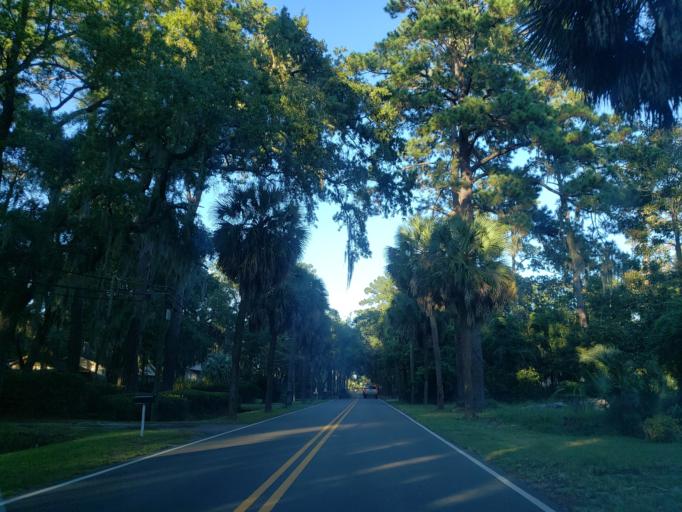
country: US
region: Georgia
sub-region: Chatham County
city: Isle of Hope
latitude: 31.9960
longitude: -81.0627
